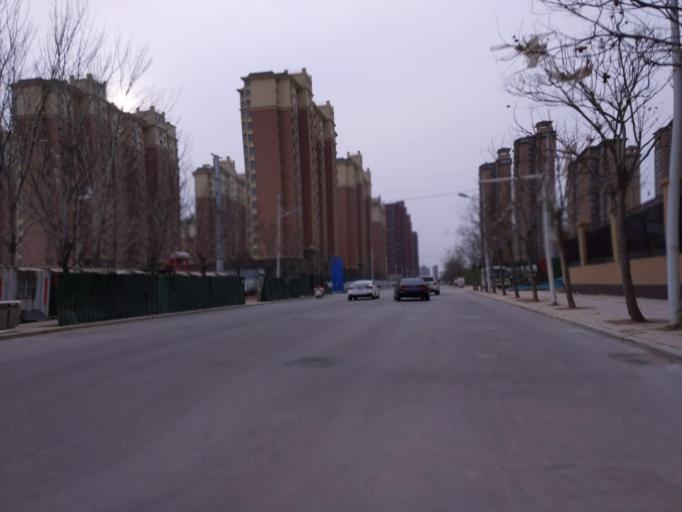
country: CN
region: Henan Sheng
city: Zhongyuanlu
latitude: 35.7426
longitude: 115.0748
